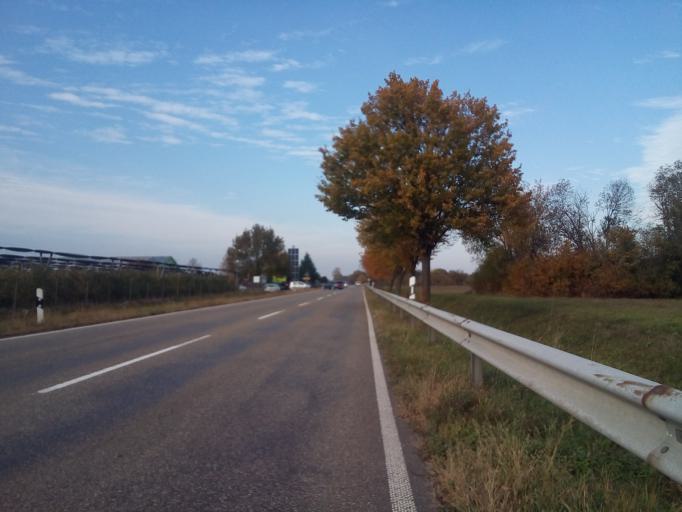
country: DE
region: Baden-Wuerttemberg
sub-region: Karlsruhe Region
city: Zell
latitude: 48.6652
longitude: 8.0602
